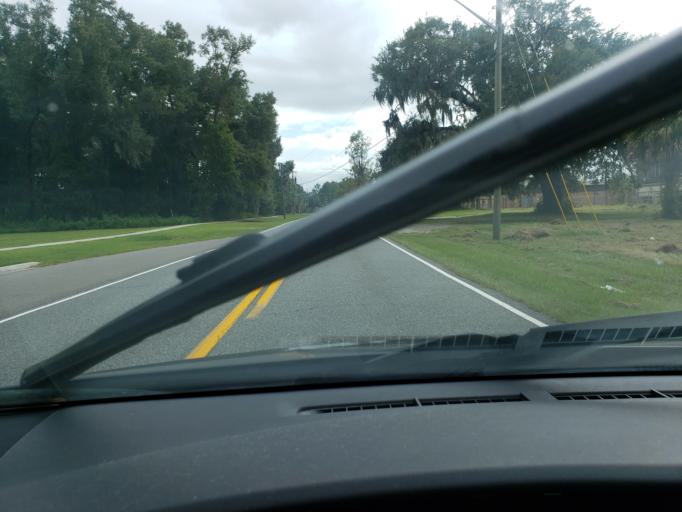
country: US
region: Georgia
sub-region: Chatham County
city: Isle of Hope
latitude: 32.0085
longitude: -81.0953
